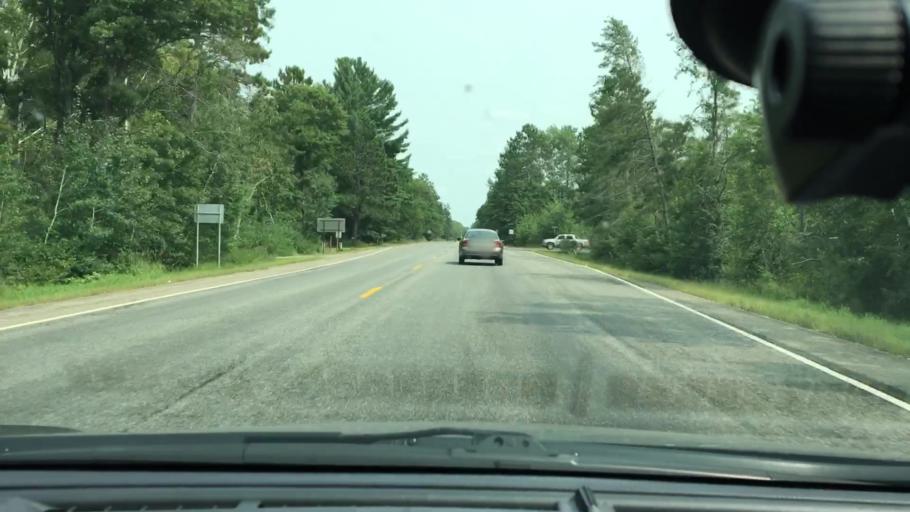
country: US
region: Minnesota
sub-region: Cass County
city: East Gull Lake
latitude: 46.4127
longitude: -94.3292
